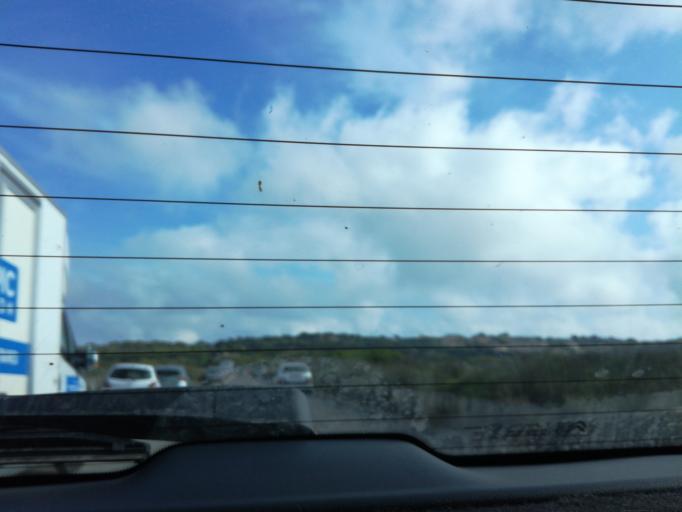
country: FR
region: Provence-Alpes-Cote d'Azur
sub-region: Departement du Var
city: Hyeres
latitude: 43.0485
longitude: 6.1332
